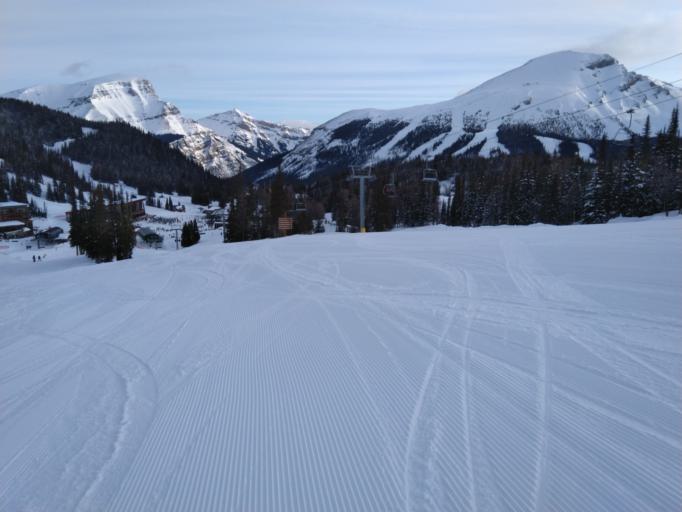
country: CA
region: Alberta
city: Banff
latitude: 51.0758
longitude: -115.7831
